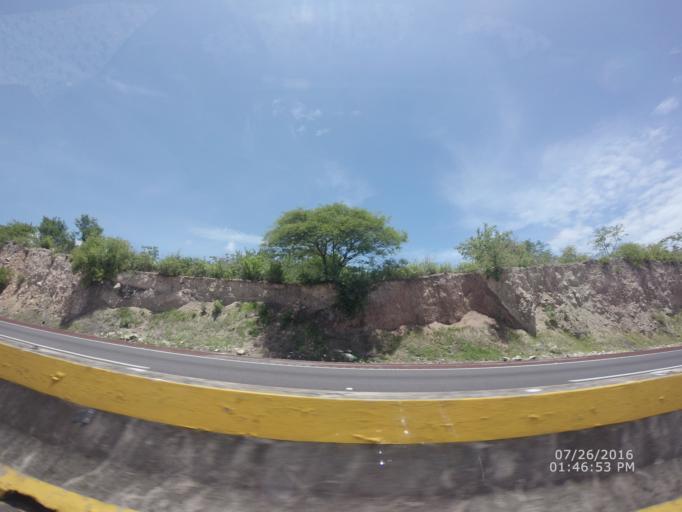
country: MX
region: Guerrero
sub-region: Huitzuco de los Figueroa
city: San Francisco Ozomatlan
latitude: 17.9972
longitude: -99.2993
